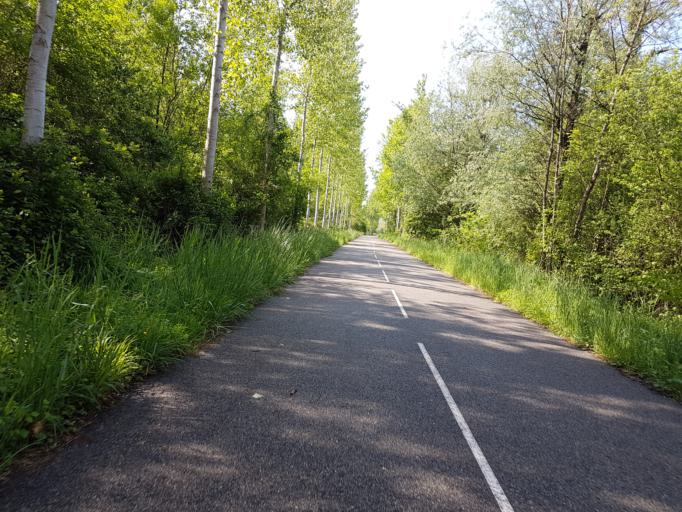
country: FR
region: Rhone-Alpes
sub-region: Departement de l'Ain
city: Culoz
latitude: 45.8568
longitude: 5.8216
